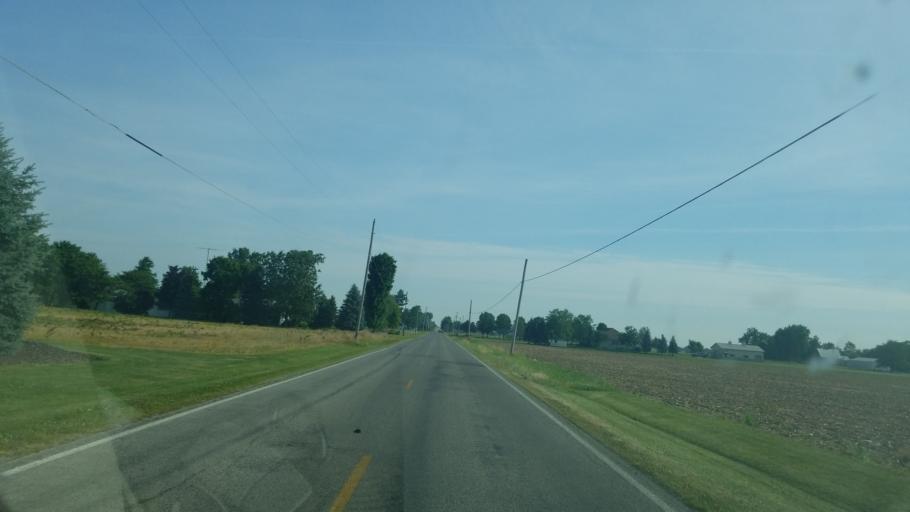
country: US
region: Ohio
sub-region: Hancock County
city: Findlay
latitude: 40.9824
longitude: -83.6985
